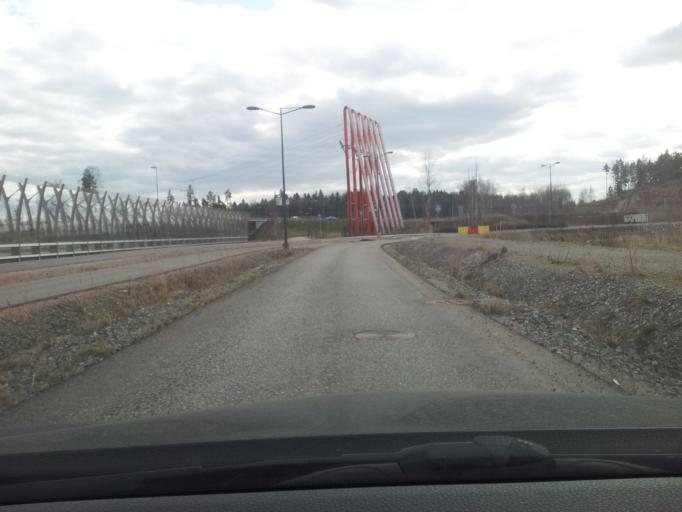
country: FI
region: Uusimaa
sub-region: Helsinki
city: Kauniainen
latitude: 60.1847
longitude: 24.7478
